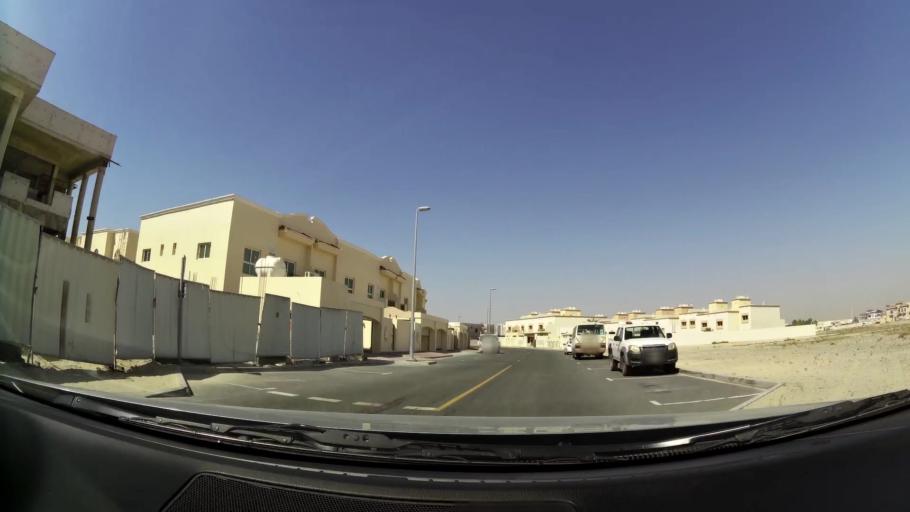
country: AE
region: Dubai
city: Dubai
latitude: 25.1039
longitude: 55.1845
